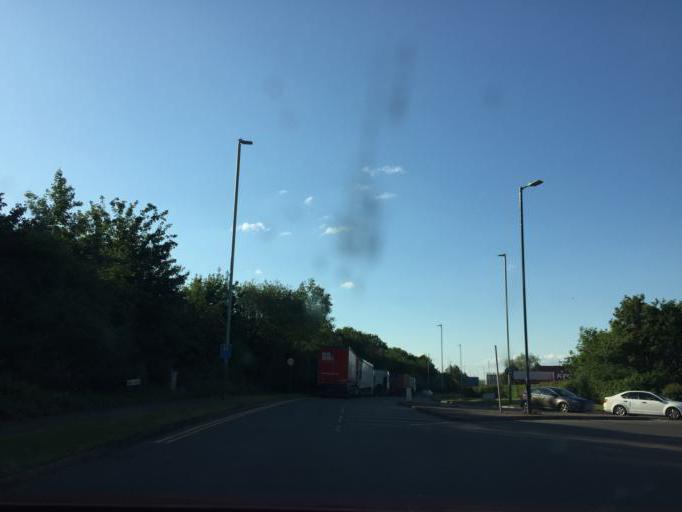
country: GB
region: England
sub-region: Warwickshire
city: Bedworth
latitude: 52.4942
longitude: -1.4798
